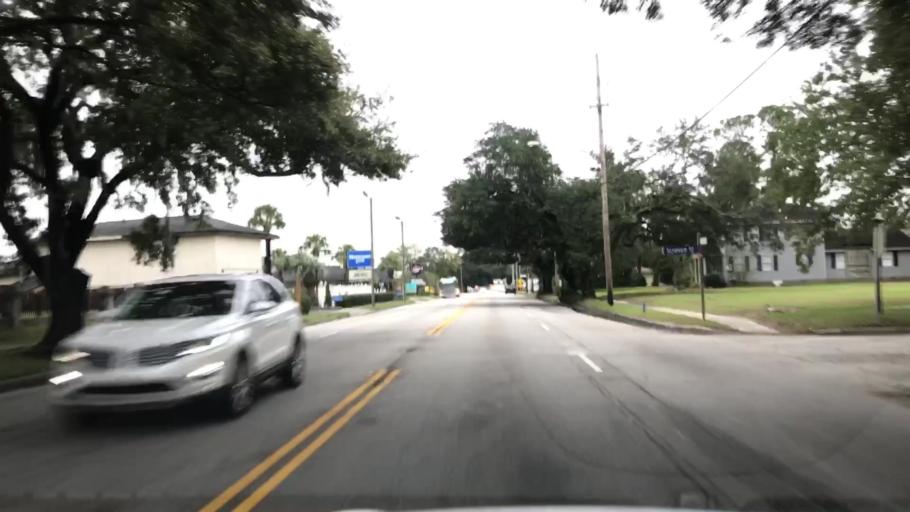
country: US
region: South Carolina
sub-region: Georgetown County
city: Georgetown
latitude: 33.3701
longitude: -79.2781
